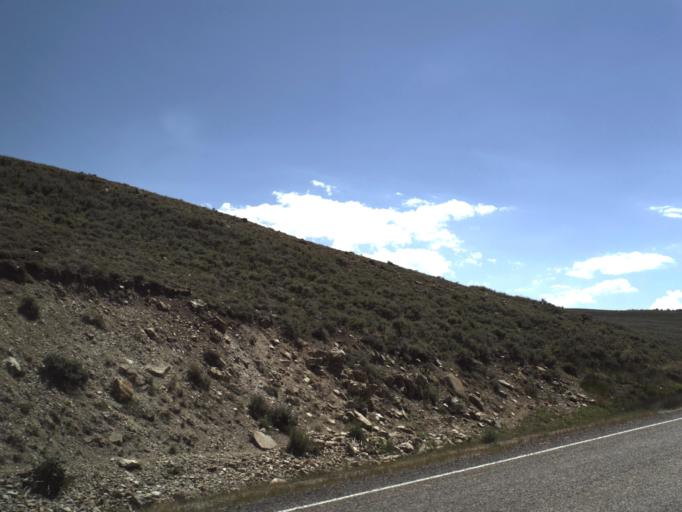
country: US
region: Utah
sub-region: Rich County
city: Randolph
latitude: 41.4840
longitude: -111.4108
